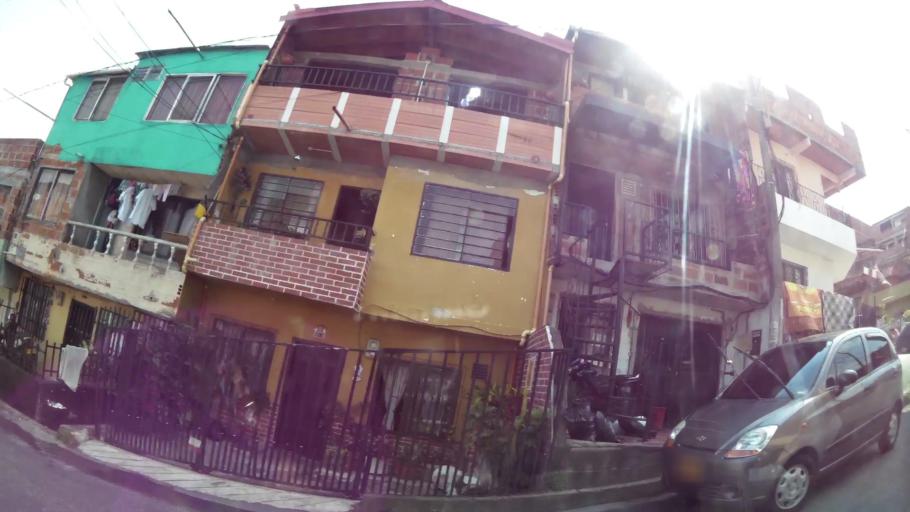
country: CO
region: Antioquia
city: Medellin
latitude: 6.2893
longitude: -75.5929
